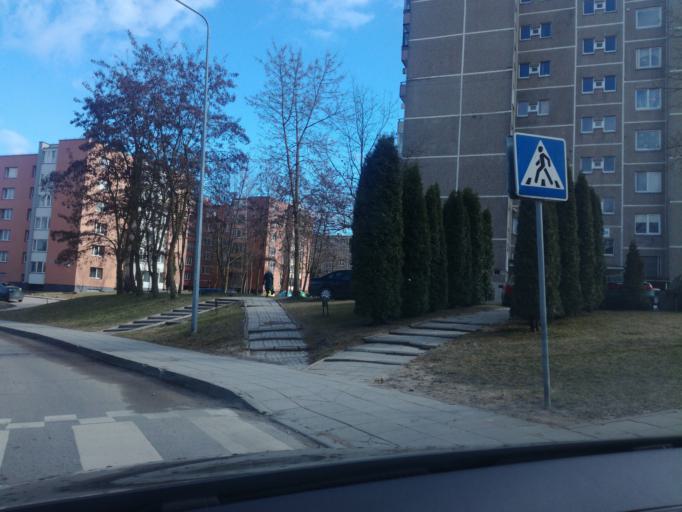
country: LT
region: Alytaus apskritis
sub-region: Alytus
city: Alytus
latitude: 54.3909
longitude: 24.0254
